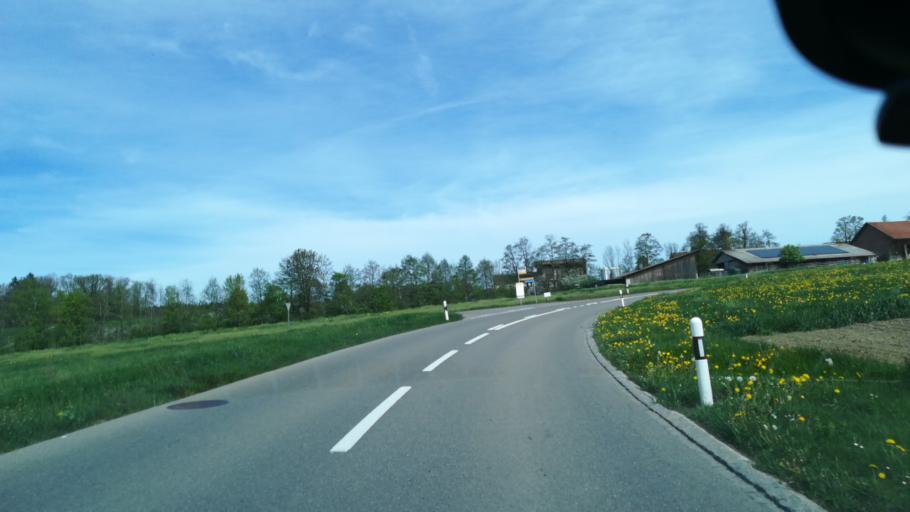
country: CH
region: Thurgau
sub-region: Weinfelden District
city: Maerstetten-Dorf
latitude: 47.6214
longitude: 9.0641
